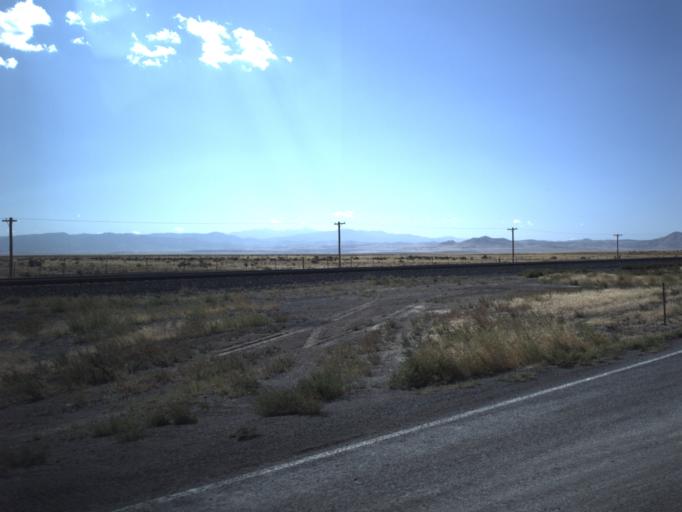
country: US
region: Utah
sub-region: Millard County
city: Delta
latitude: 38.9378
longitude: -112.8085
